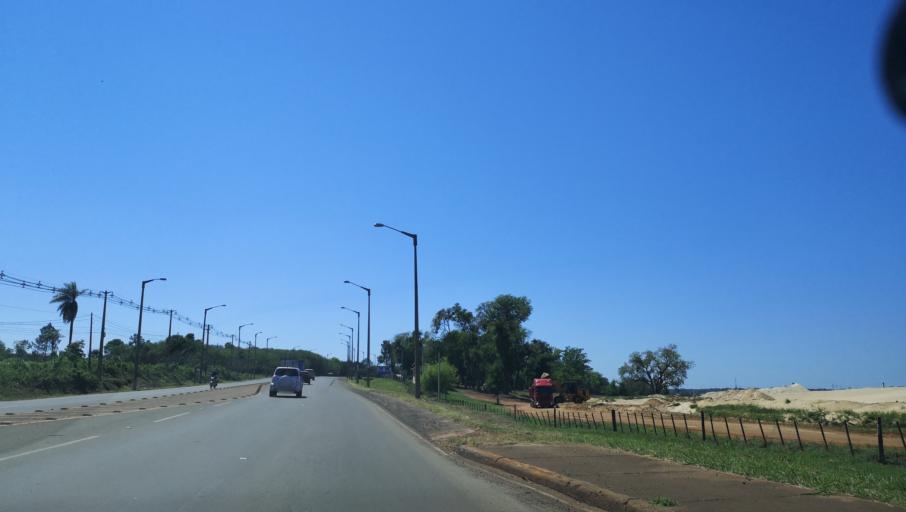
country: PY
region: Itapua
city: San Juan del Parana
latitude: -27.2920
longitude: -55.9192
